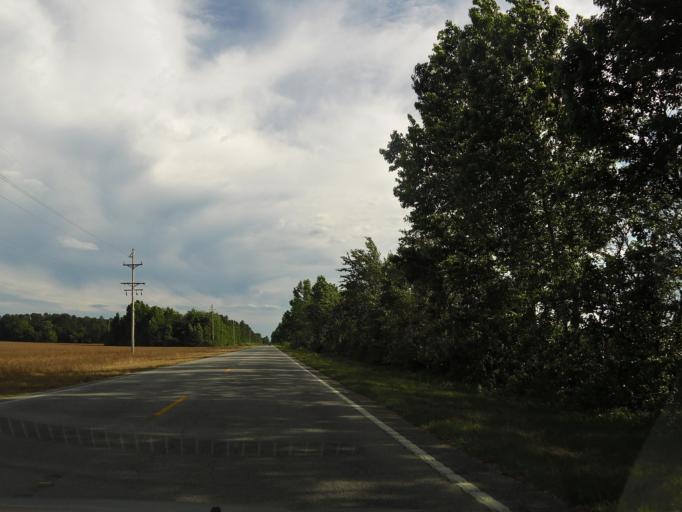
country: US
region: South Carolina
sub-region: Hampton County
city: Estill
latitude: 32.8293
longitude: -81.2396
